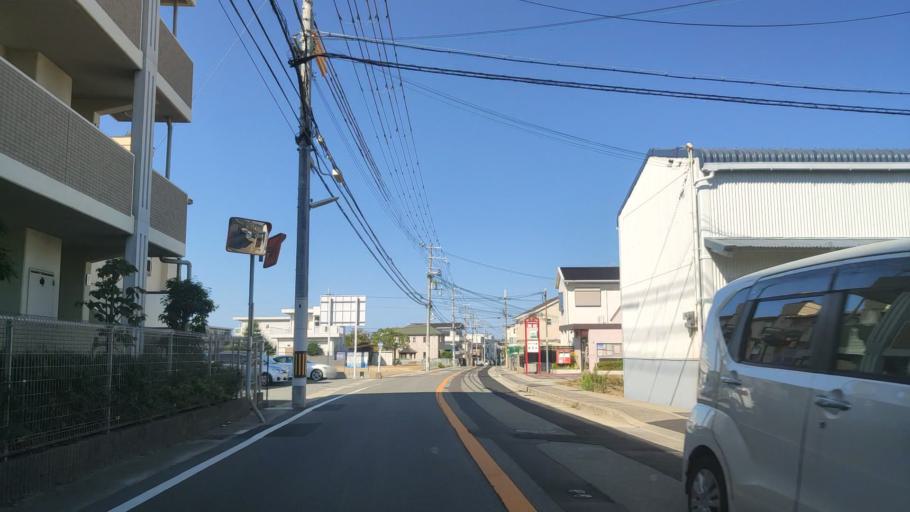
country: JP
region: Hyogo
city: Akashi
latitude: 34.6607
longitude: 135.0204
